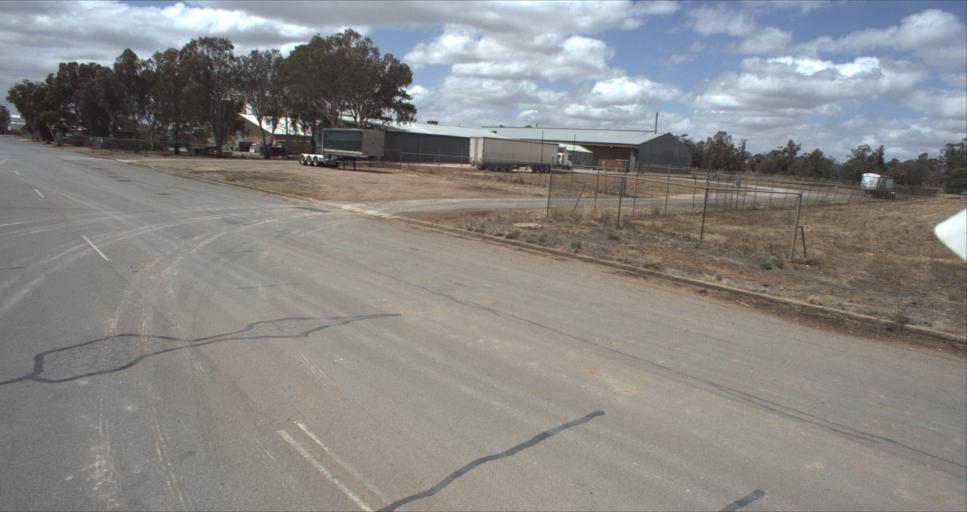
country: AU
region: New South Wales
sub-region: Leeton
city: Leeton
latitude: -34.5581
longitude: 146.3913
